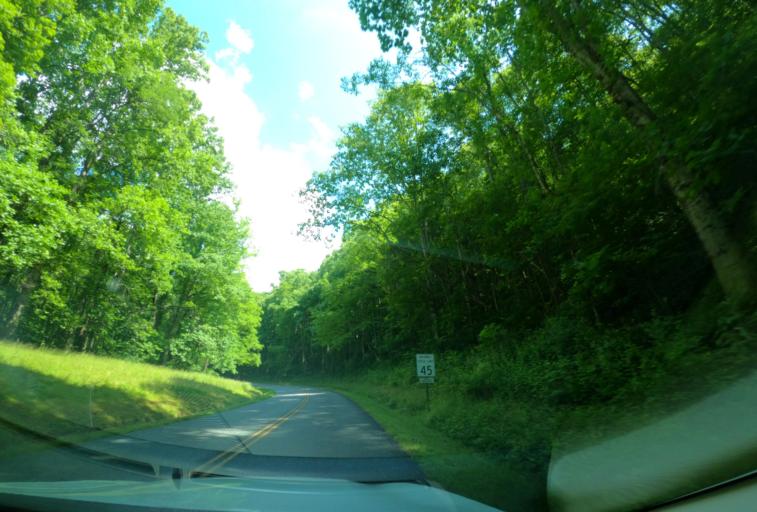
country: US
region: North Carolina
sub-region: Haywood County
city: Maggie Valley
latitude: 35.4432
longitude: -83.0809
